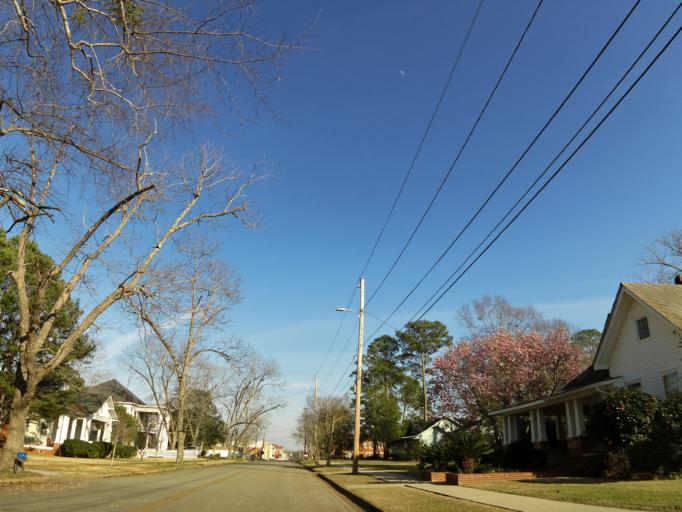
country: US
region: Georgia
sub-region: Stewart County
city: Richland
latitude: 32.0898
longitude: -84.6692
